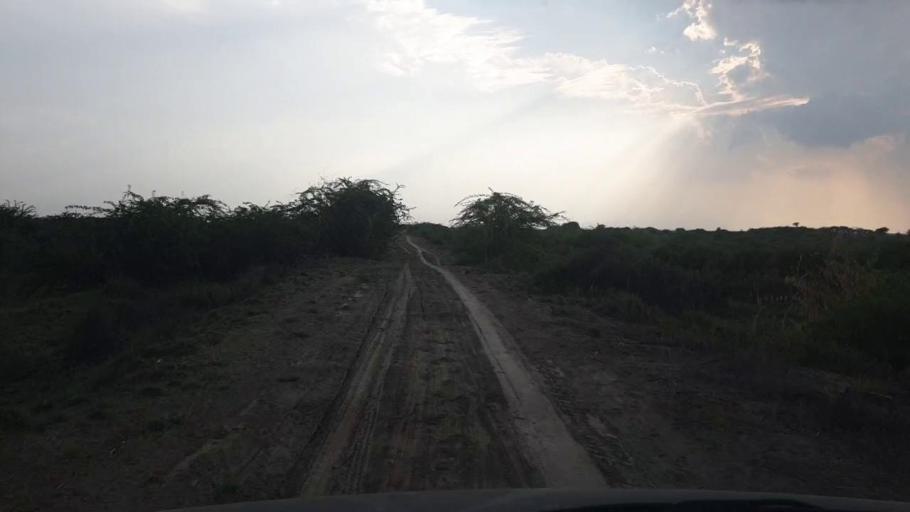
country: PK
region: Sindh
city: Badin
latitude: 24.4689
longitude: 68.6954
